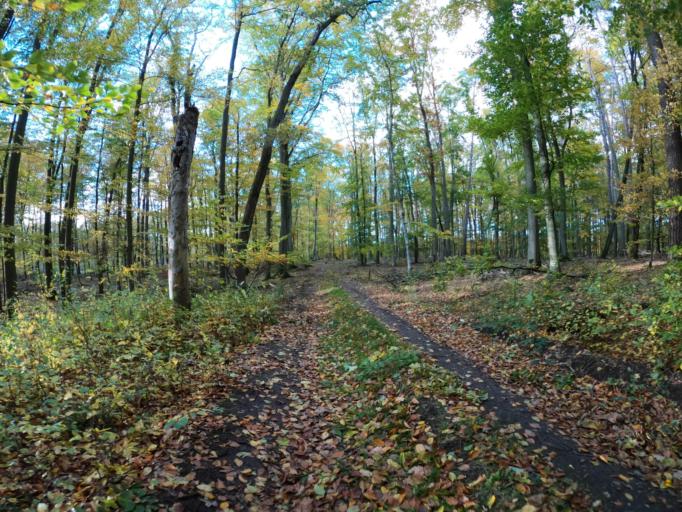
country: PL
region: West Pomeranian Voivodeship
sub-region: Powiat mysliborski
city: Barlinek
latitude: 52.9475
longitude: 15.2720
